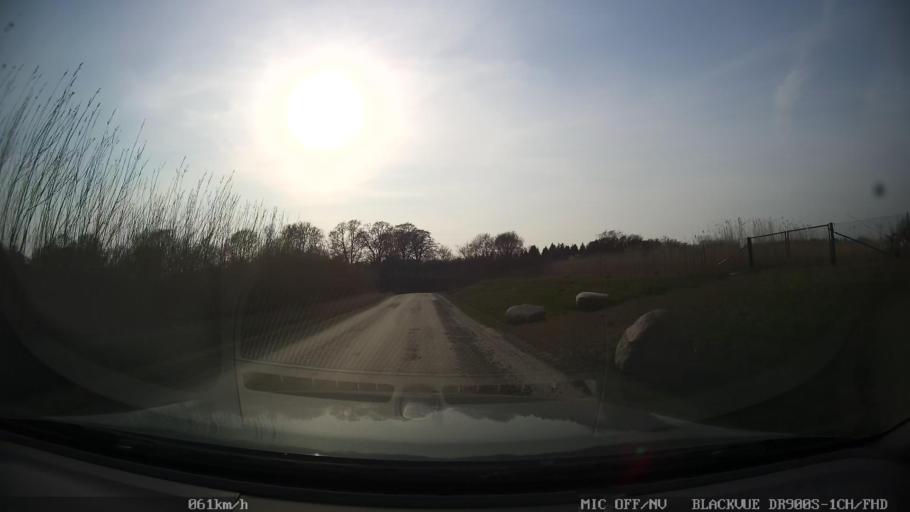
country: SE
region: Skane
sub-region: Ystads Kommun
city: Ystad
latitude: 55.4599
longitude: 13.7847
